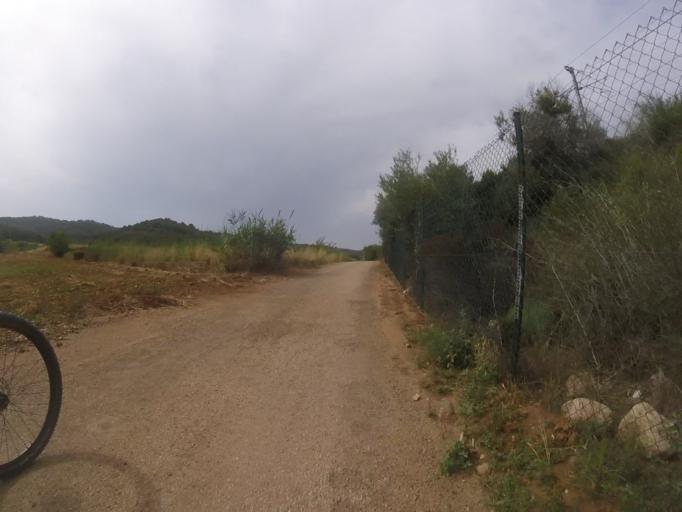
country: ES
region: Valencia
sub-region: Provincia de Castello
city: Alcoceber
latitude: 40.2612
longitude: 0.2551
